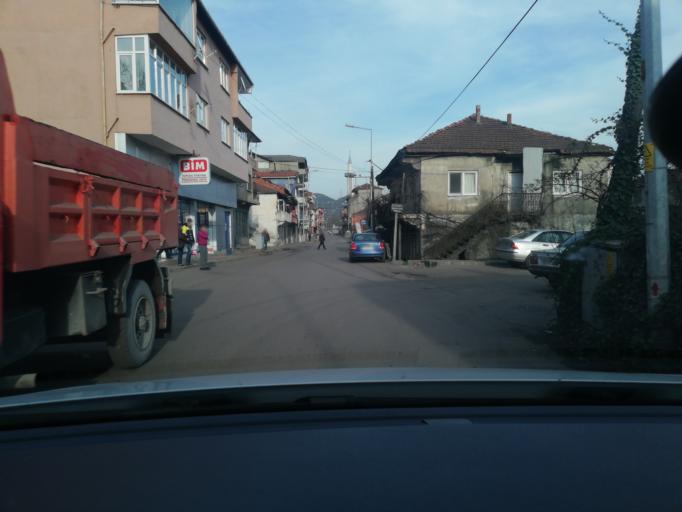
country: TR
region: Zonguldak
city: Kilimli
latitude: 41.4984
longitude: 31.8667
